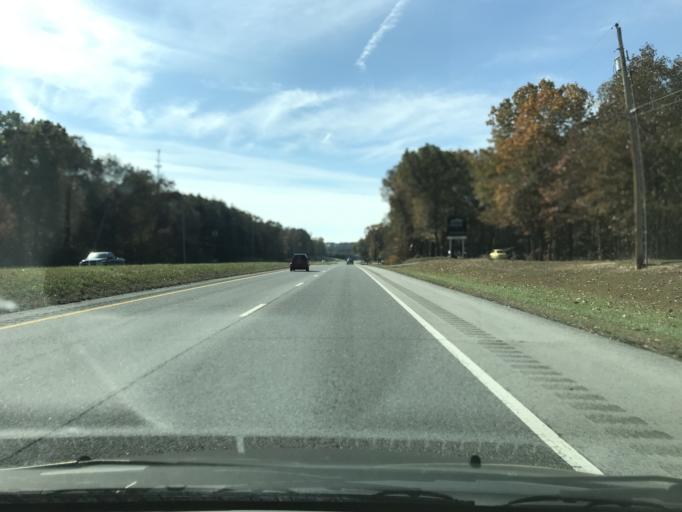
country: US
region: Tennessee
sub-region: Coffee County
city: Manchester
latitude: 35.4198
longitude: -86.1136
